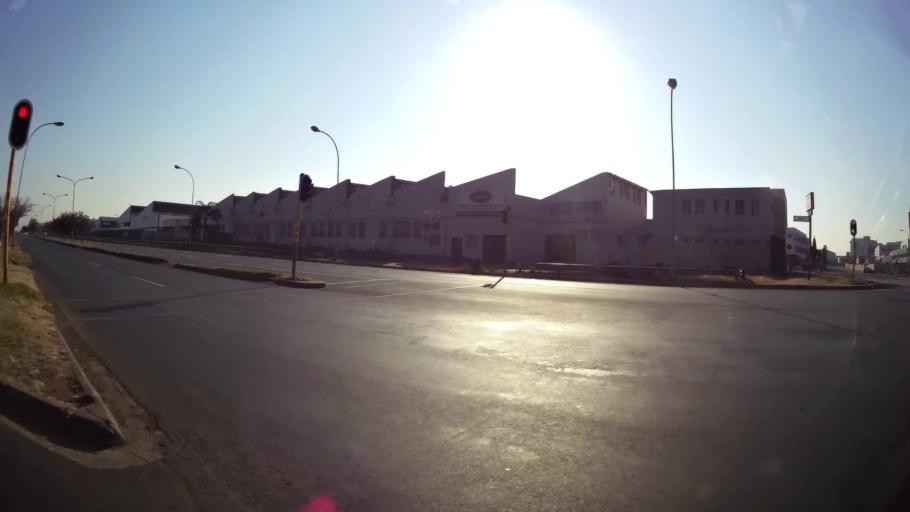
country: ZA
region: Gauteng
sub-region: City of Johannesburg Metropolitan Municipality
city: Modderfontein
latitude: -26.1486
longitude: 28.2008
